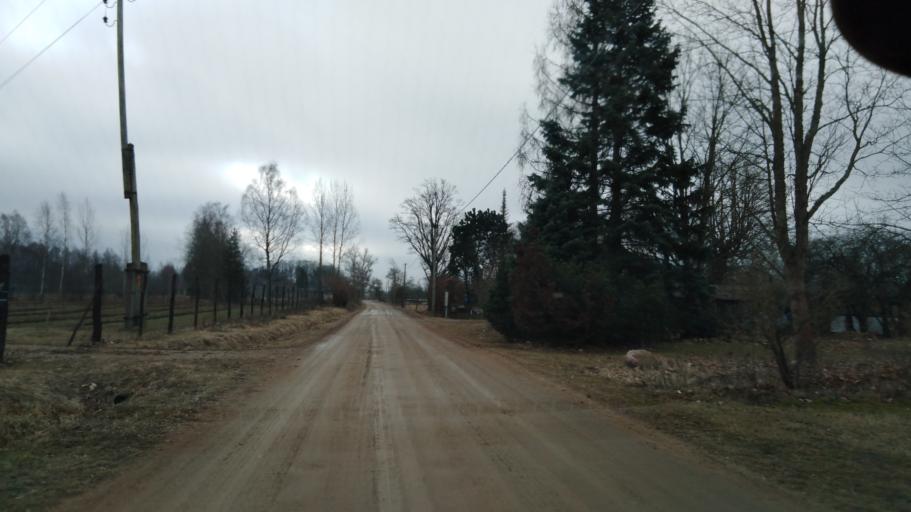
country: LV
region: Kuldigas Rajons
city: Kuldiga
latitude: 56.9869
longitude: 21.9702
